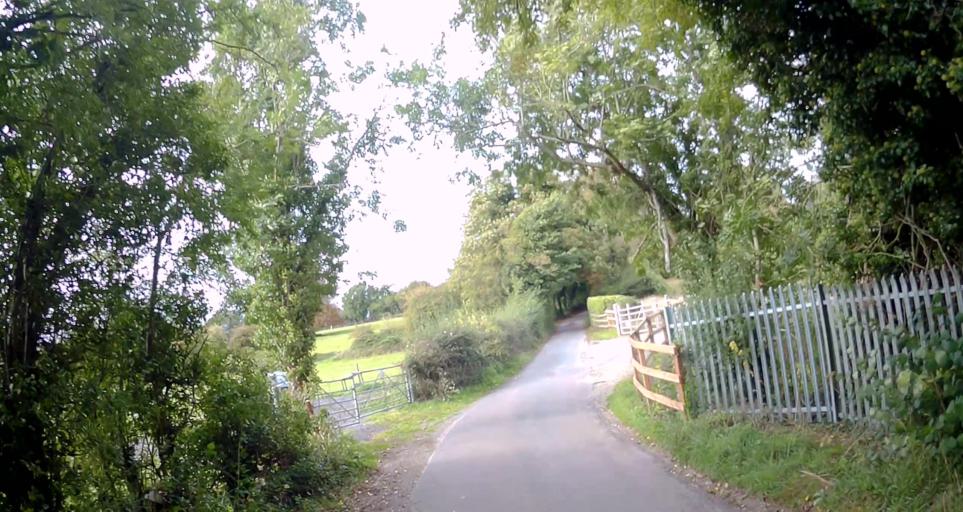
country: GB
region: England
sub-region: Hampshire
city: Kings Worthy
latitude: 51.0897
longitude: -1.1814
